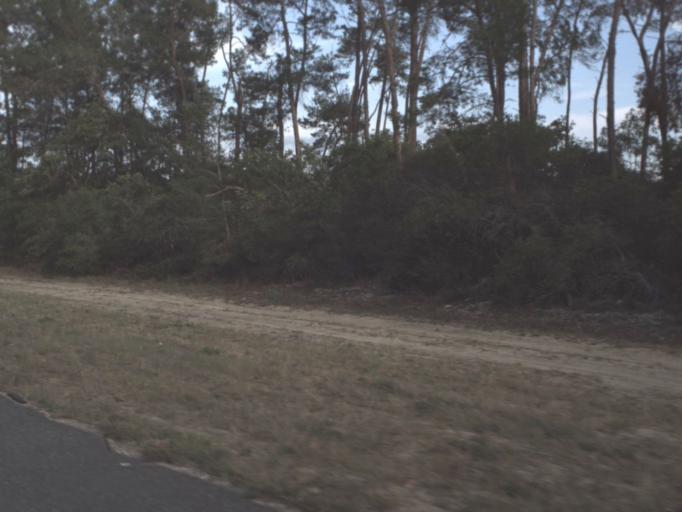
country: US
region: Florida
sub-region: Lake County
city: Astor
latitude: 29.1772
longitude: -81.7757
